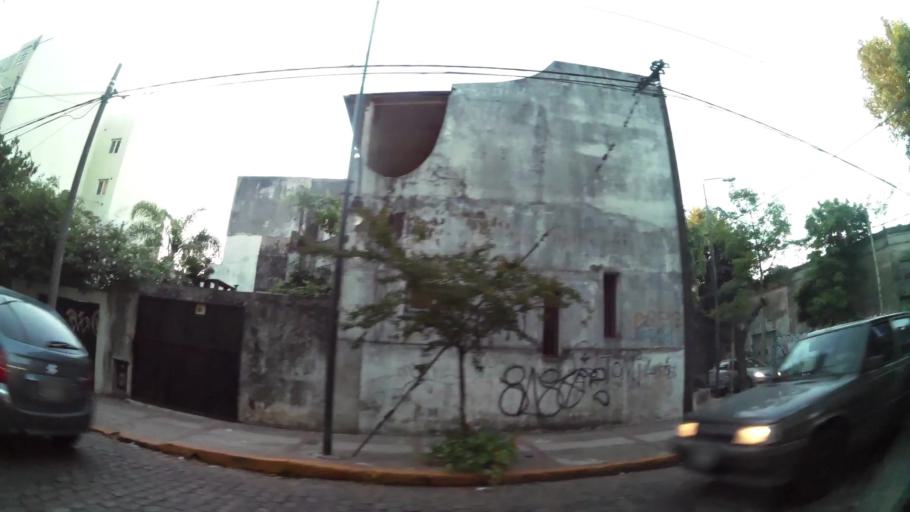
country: AR
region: Buenos Aires
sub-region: Partido de Tigre
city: Tigre
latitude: -34.4407
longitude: -58.5620
